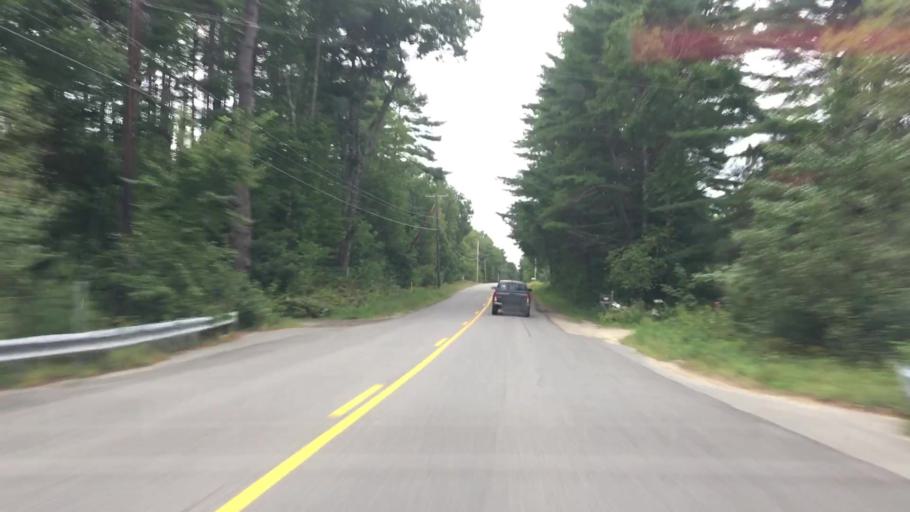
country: US
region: Maine
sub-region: Cumberland County
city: Freeport
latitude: 43.8830
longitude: -70.1654
